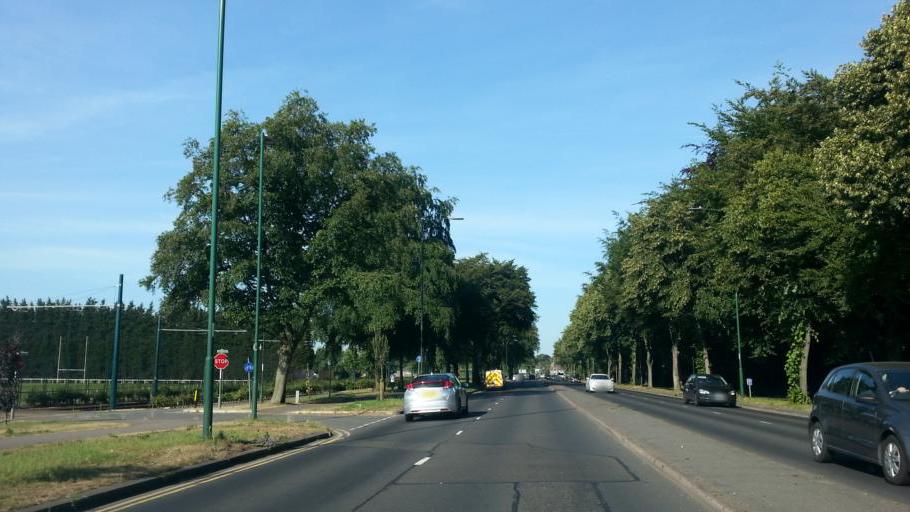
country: GB
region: England
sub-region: Nottingham
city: Nottingham
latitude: 52.9339
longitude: -1.1964
